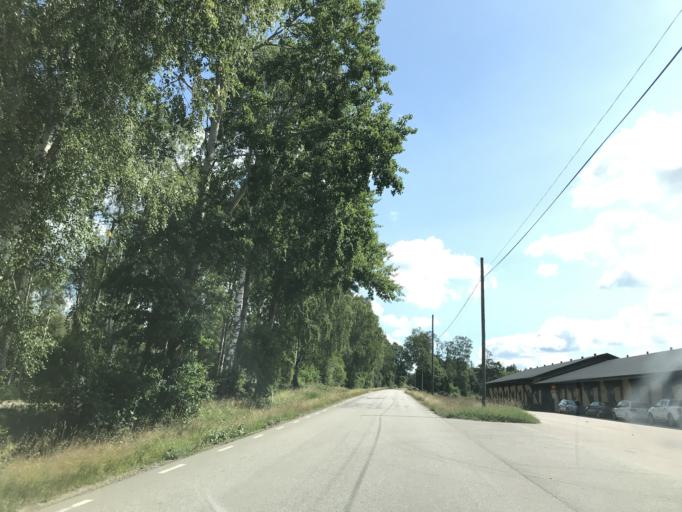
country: SE
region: Halland
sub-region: Laholms Kommun
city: Knared
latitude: 56.5198
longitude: 13.3416
